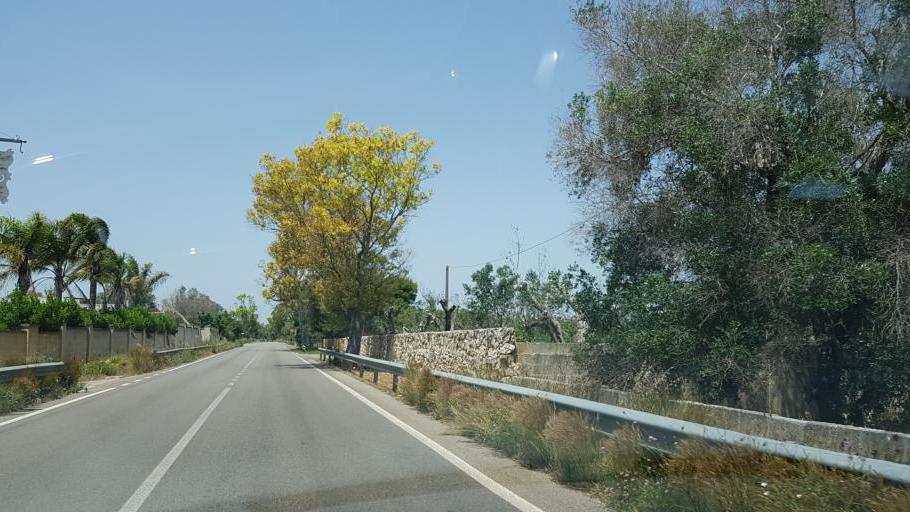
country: IT
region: Apulia
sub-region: Provincia di Lecce
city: Porto Cesareo
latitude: 40.2566
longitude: 17.9268
